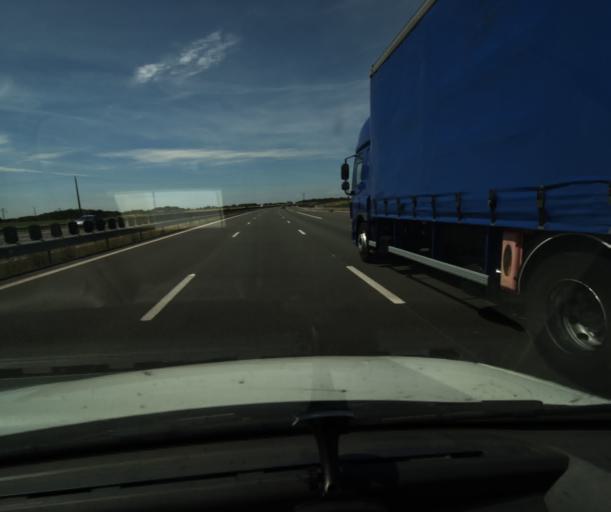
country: FR
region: Midi-Pyrenees
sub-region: Departement du Tarn-et-Garonne
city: Pompignan
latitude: 43.8453
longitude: 1.3236
